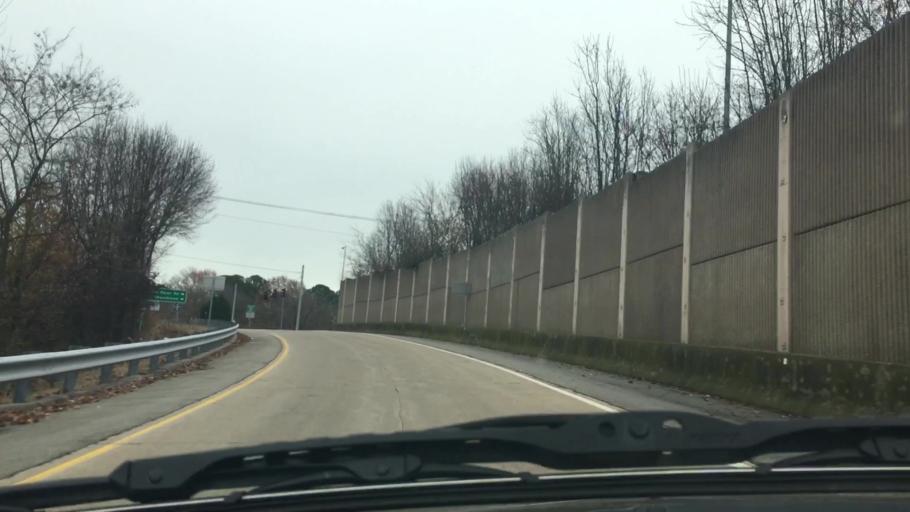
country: US
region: Virginia
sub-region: City of Portsmouth
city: Portsmouth Heights
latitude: 36.8691
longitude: -76.4021
